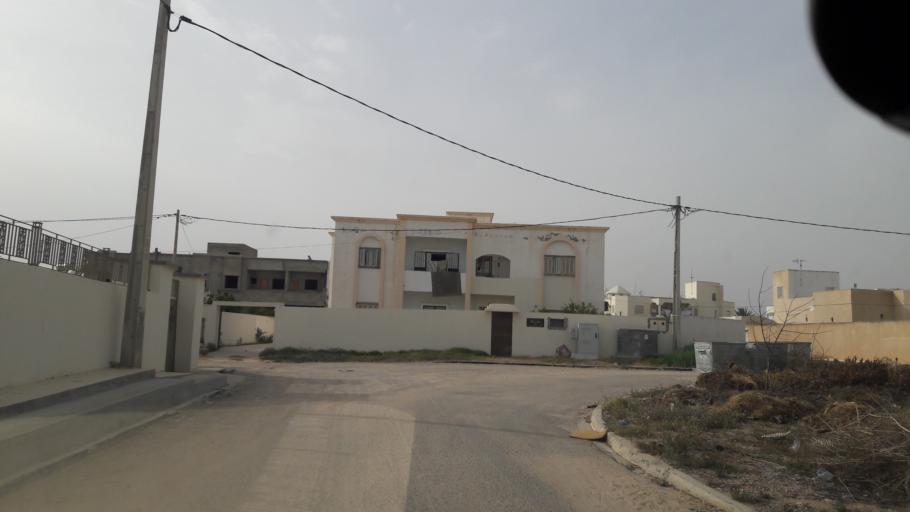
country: TN
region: Safaqis
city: Al Qarmadah
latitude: 34.7795
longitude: 10.7670
